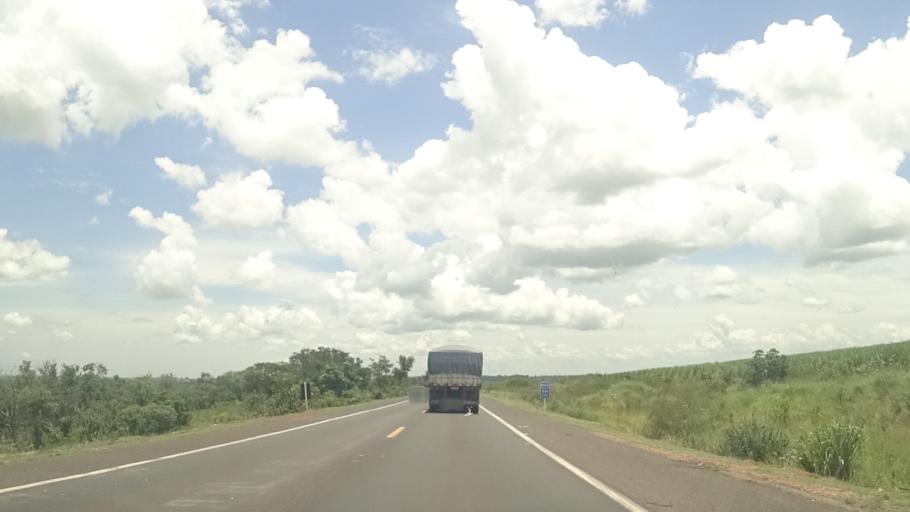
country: BR
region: Minas Gerais
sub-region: Prata
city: Prata
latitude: -19.5374
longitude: -48.8300
